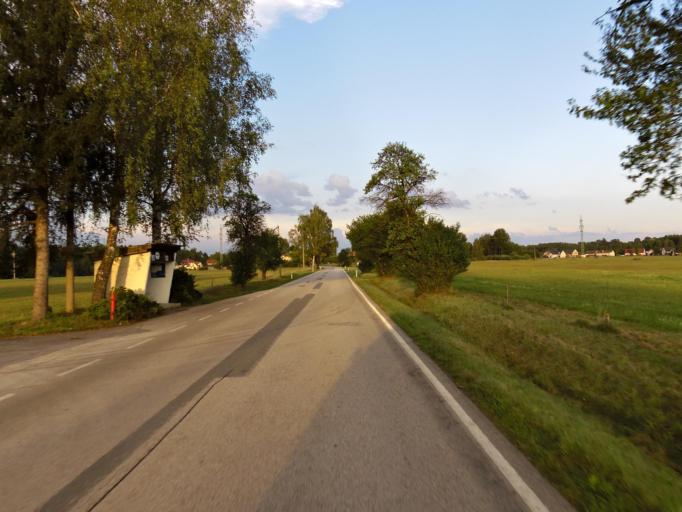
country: CZ
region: Jihocesky
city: Chlum u Trebone
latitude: 48.9512
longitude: 14.9049
